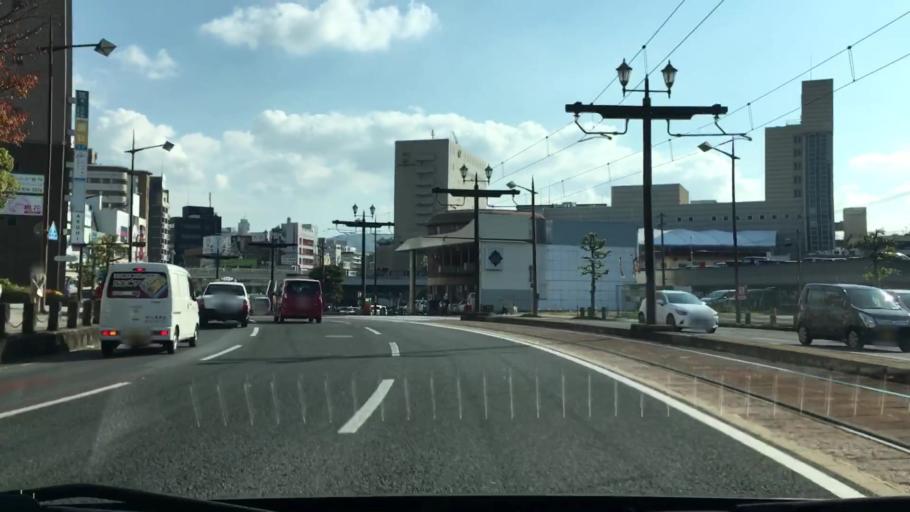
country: JP
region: Nagasaki
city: Nagasaki-shi
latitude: 32.7540
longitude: 129.8707
